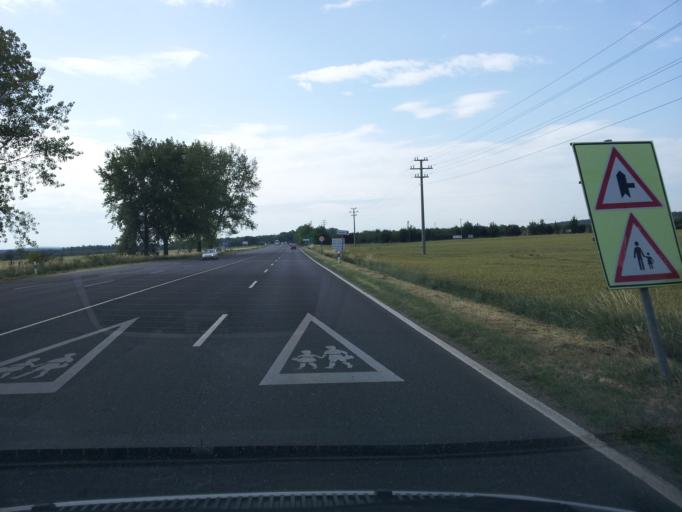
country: HU
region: Veszprem
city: Veszprem
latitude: 47.0634
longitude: 17.9233
